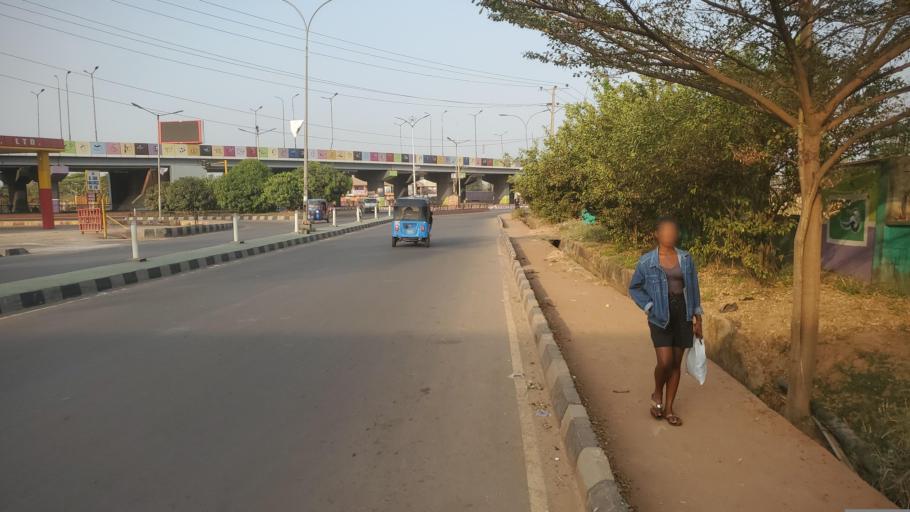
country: NG
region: Ebonyi
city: Abakaliki
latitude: 6.3258
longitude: 8.0850
